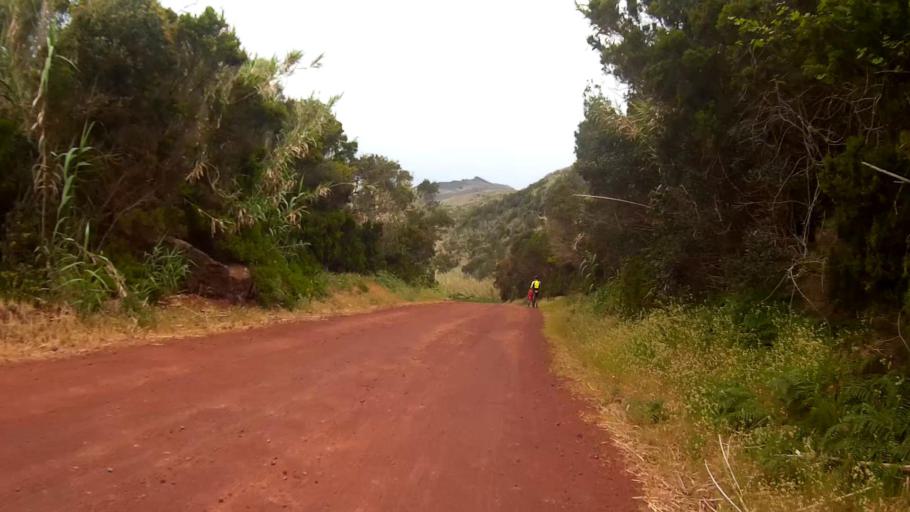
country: PT
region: Azores
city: Ribeira Grande
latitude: 38.5863
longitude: -28.8182
